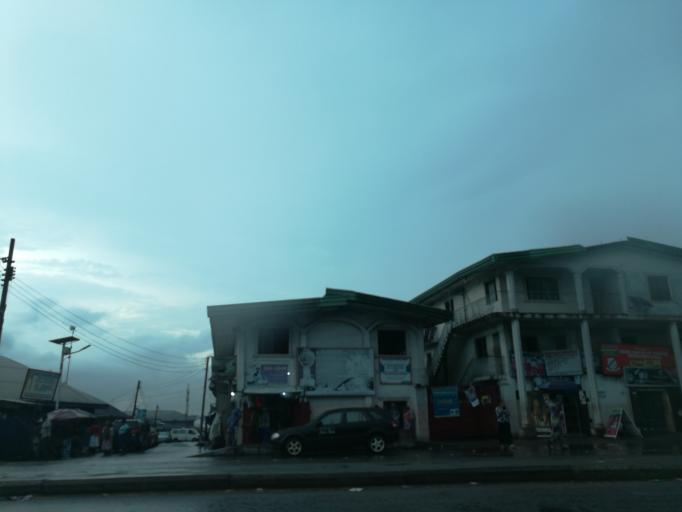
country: NG
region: Rivers
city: Port Harcourt
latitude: 4.8001
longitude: 6.9911
